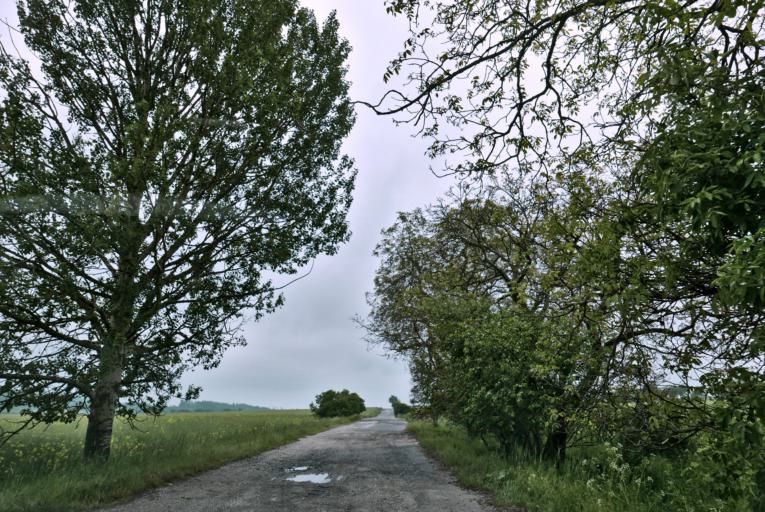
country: CZ
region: Plzensky
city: Zihle
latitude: 50.0199
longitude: 13.3282
